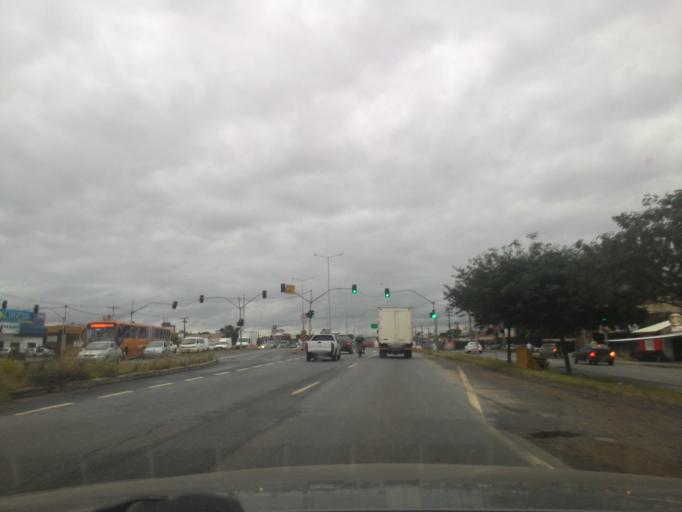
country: BR
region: Parana
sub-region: Sao Jose Dos Pinhais
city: Sao Jose dos Pinhais
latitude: -25.5267
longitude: -49.2976
